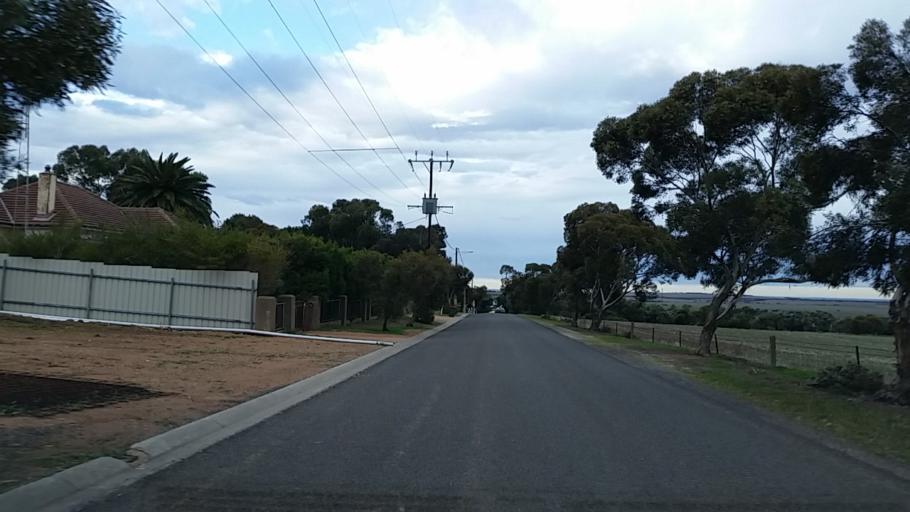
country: AU
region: South Australia
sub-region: Mid Murray
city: Mannum
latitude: -34.8534
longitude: 139.1597
